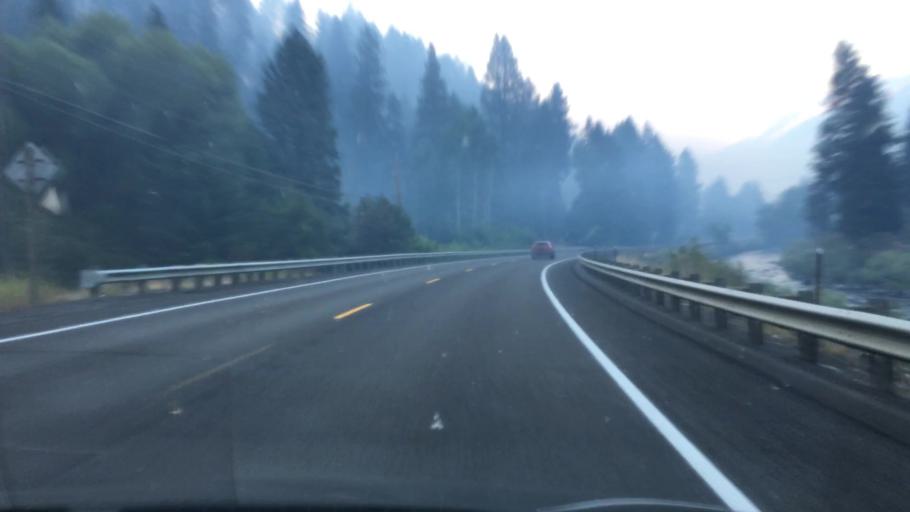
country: US
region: Idaho
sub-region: Valley County
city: McCall
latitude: 45.2402
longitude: -116.3315
